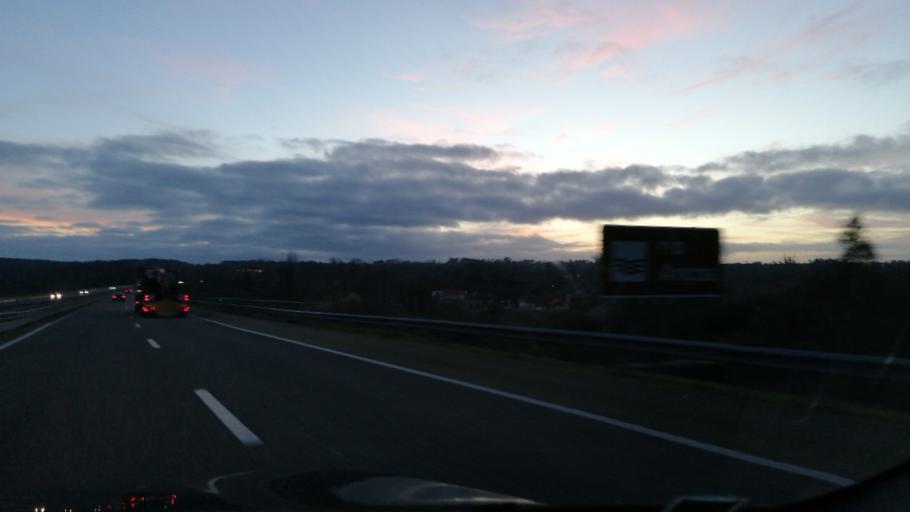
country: PT
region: Coimbra
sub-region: Soure
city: Soure
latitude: 40.0274
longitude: -8.5886
